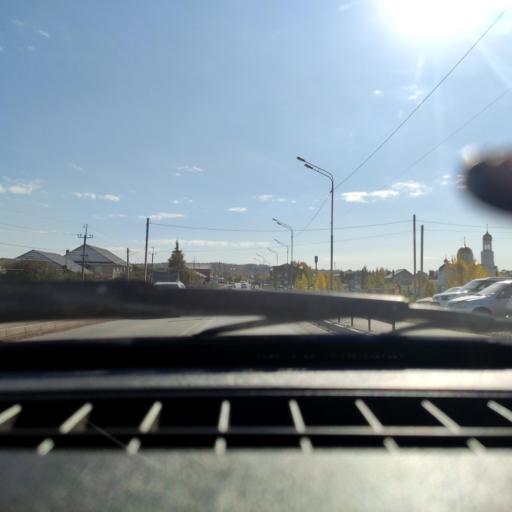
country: RU
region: Bashkortostan
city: Ufa
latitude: 54.6150
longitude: 55.9349
